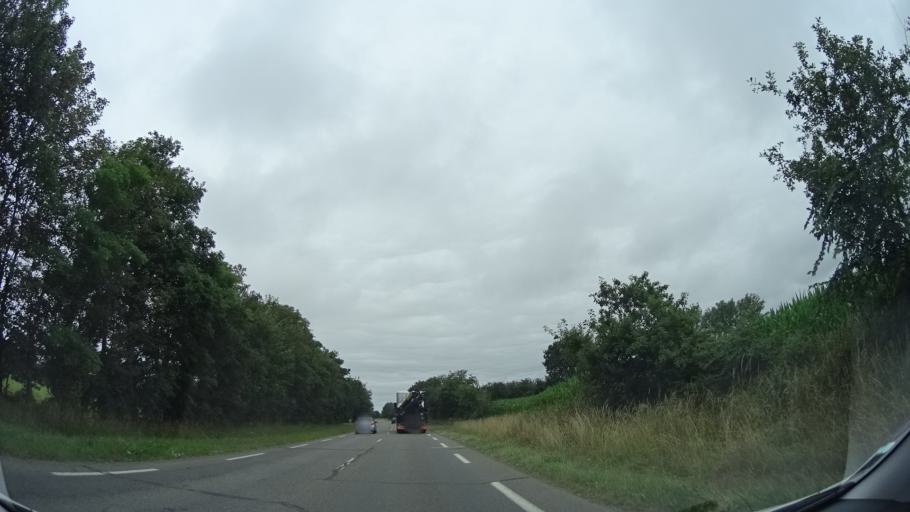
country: FR
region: Lower Normandy
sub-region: Departement de la Manche
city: Portbail
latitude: 49.3621
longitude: -1.6989
